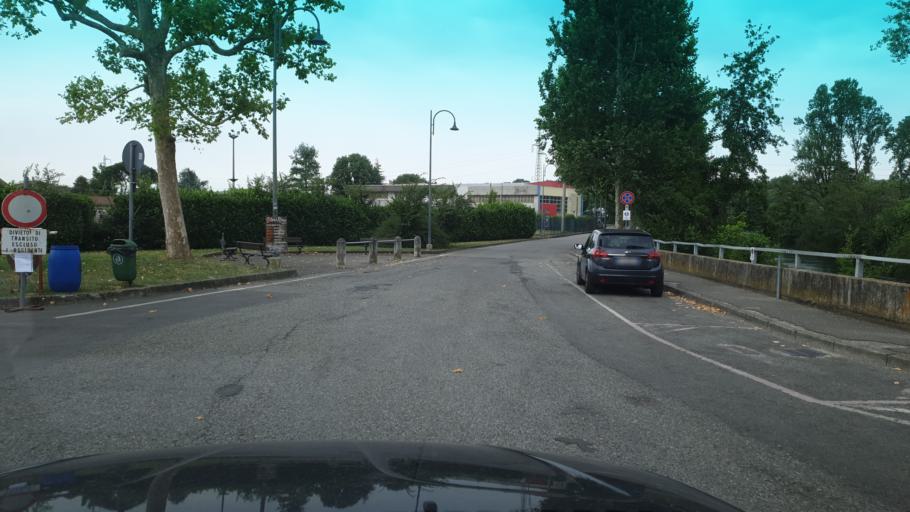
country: IT
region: Lombardy
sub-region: Provincia di Bergamo
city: Fara Gera d'Adda
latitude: 45.5520
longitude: 9.5299
